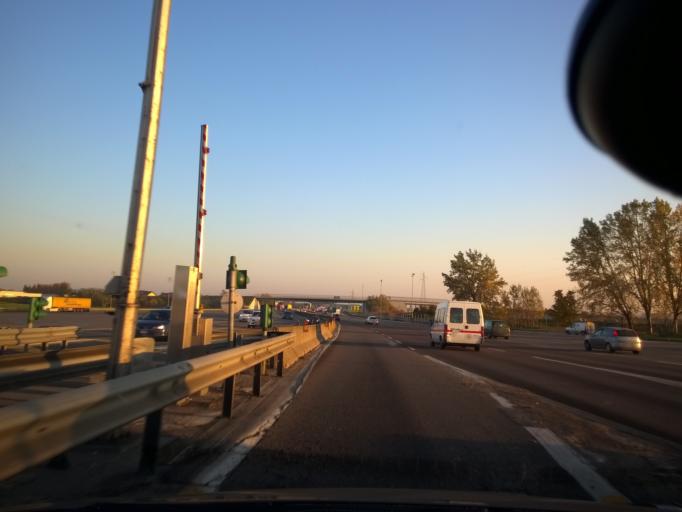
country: IT
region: Lombardy
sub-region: Citta metropolitana di Milano
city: Riozzo
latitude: 45.3487
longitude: 9.3100
